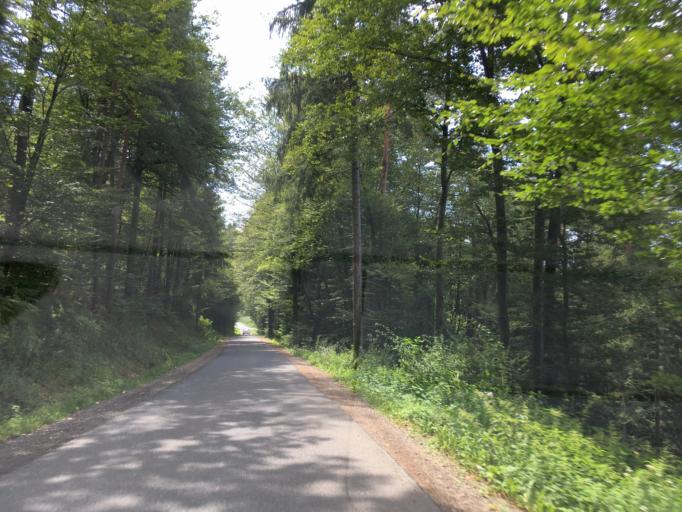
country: AT
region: Styria
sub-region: Politischer Bezirk Leibnitz
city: Pistorf
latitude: 46.7696
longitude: 15.3927
